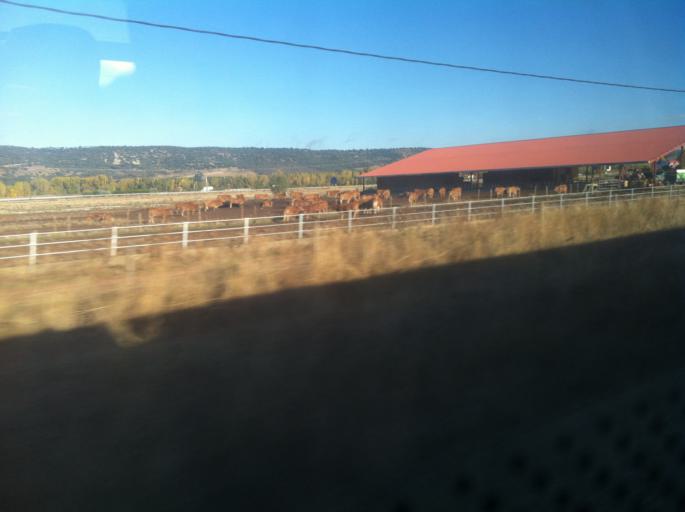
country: ES
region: Castille and Leon
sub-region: Provincia de Palencia
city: Quintana del Puente
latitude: 42.0665
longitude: -4.2197
